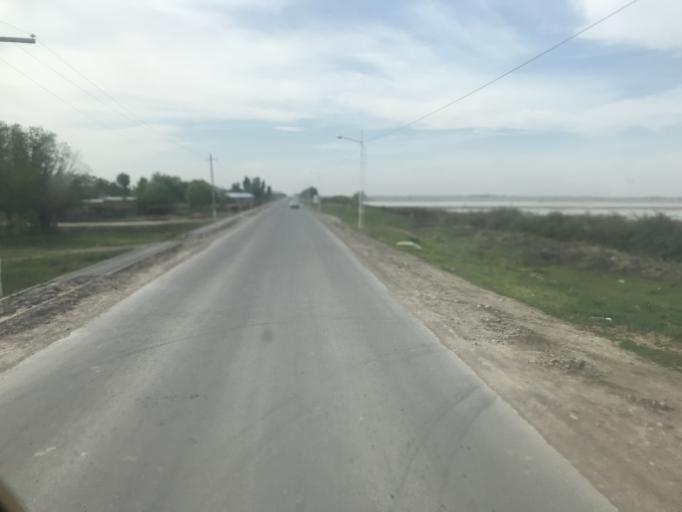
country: KZ
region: Ongtustik Qazaqstan
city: Asykata
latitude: 41.0017
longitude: 68.2136
